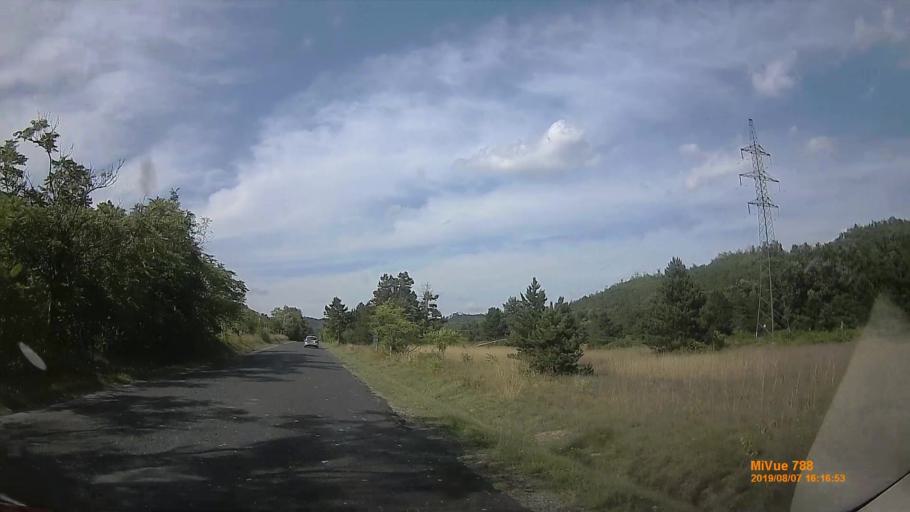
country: HU
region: Zala
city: Gyenesdias
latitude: 46.8187
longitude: 17.2706
